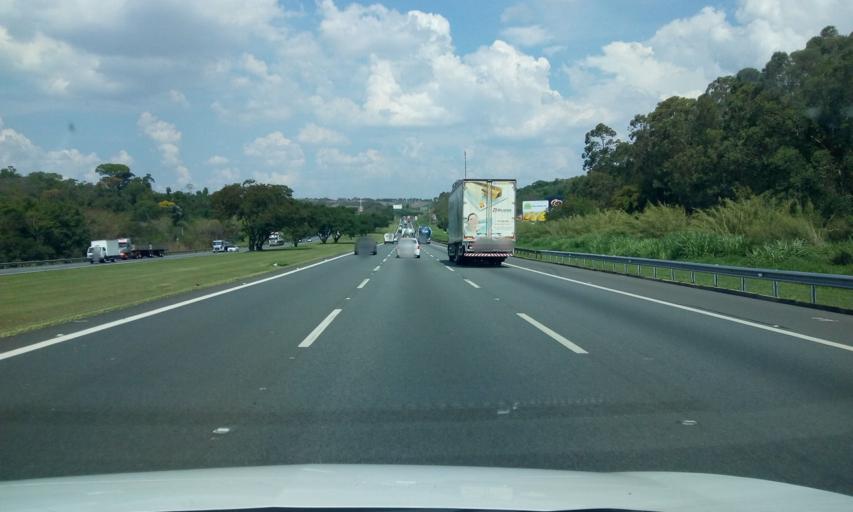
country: BR
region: Sao Paulo
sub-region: Vinhedo
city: Vinhedo
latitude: -23.0638
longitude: -47.0382
